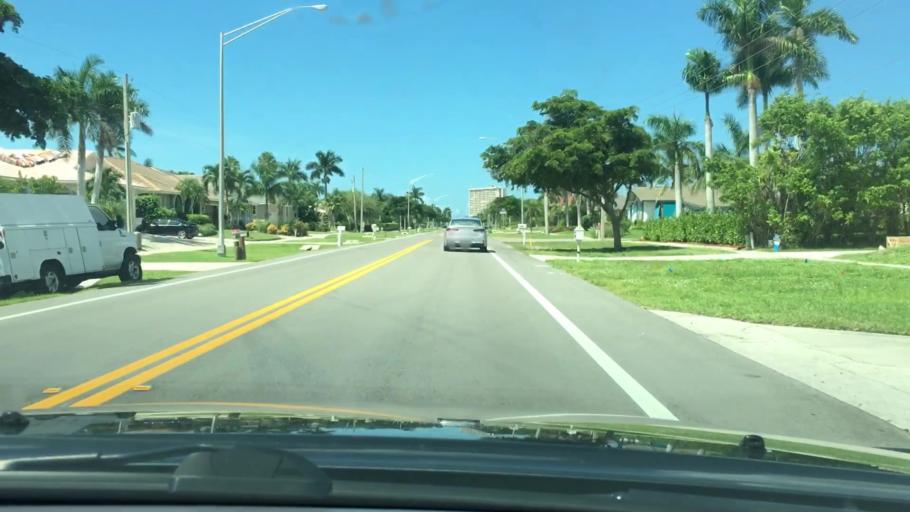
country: US
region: Florida
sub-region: Collier County
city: Marco
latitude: 25.9371
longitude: -81.7188
